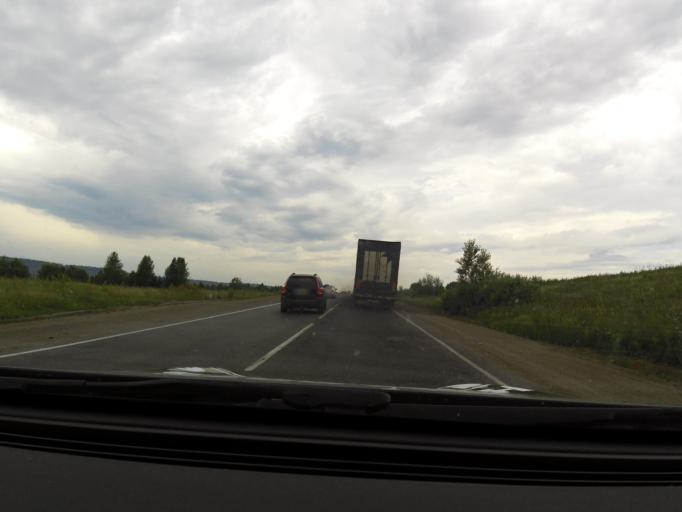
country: RU
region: Chelyabinsk
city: Sim
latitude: 55.0057
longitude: 57.6749
